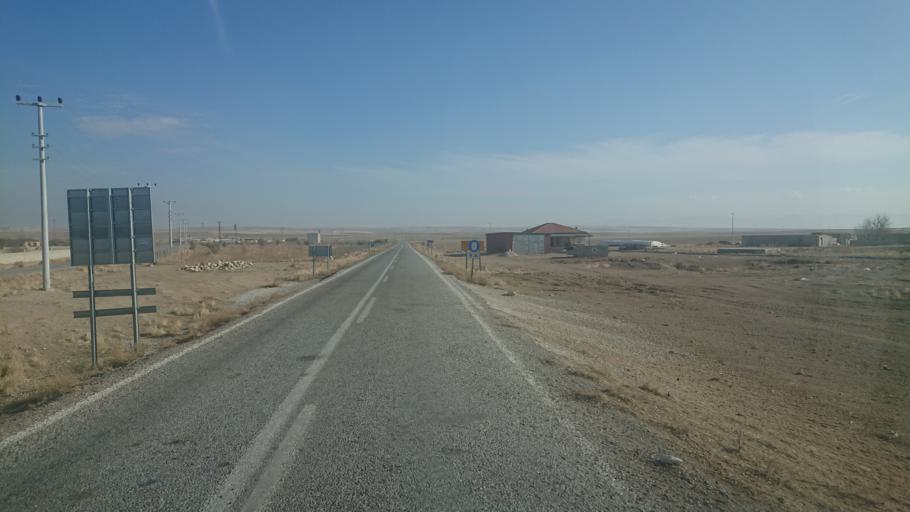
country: TR
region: Aksaray
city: Sultanhani
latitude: 38.0392
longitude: 33.5961
